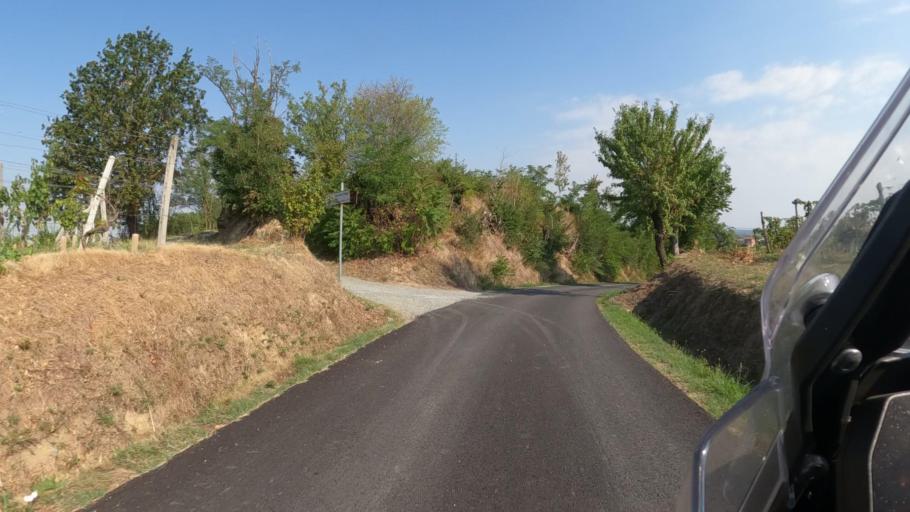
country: IT
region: Piedmont
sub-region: Provincia di Asti
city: Castel Boglione
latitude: 44.7522
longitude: 8.3830
